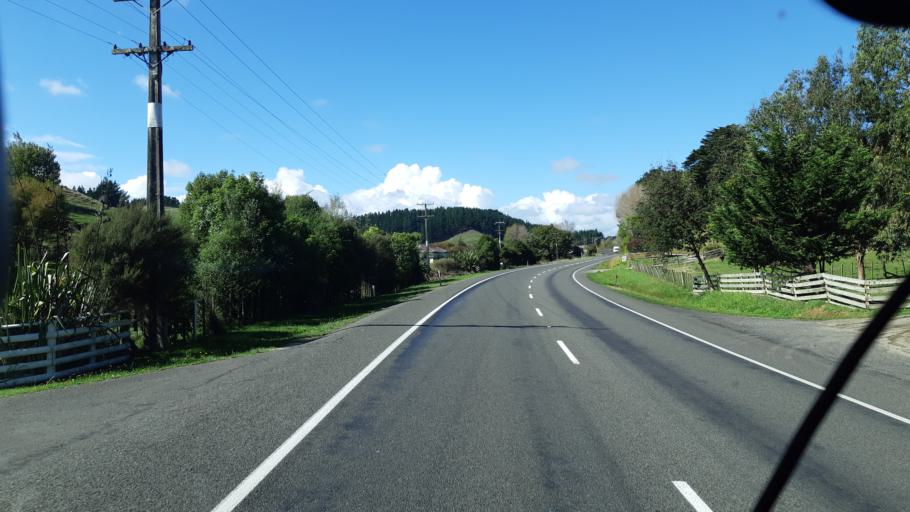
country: NZ
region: Manawatu-Wanganui
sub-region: Wanganui District
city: Wanganui
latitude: -39.9594
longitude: 175.0926
